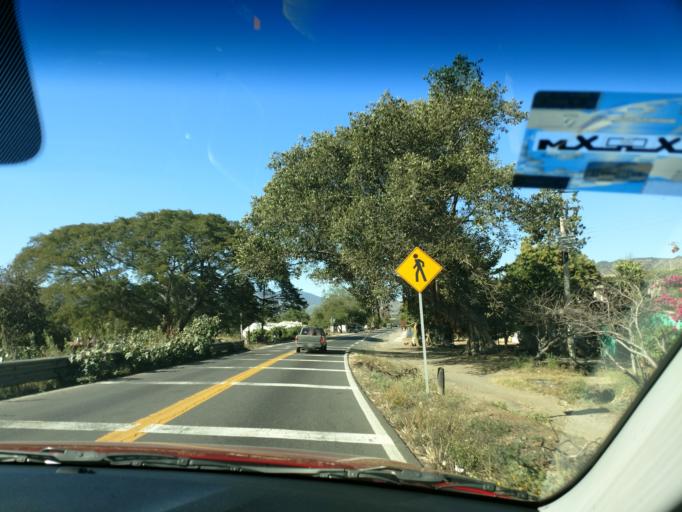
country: MX
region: Nayarit
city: San Pedro Lagunillas
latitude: 21.1552
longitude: -104.6245
